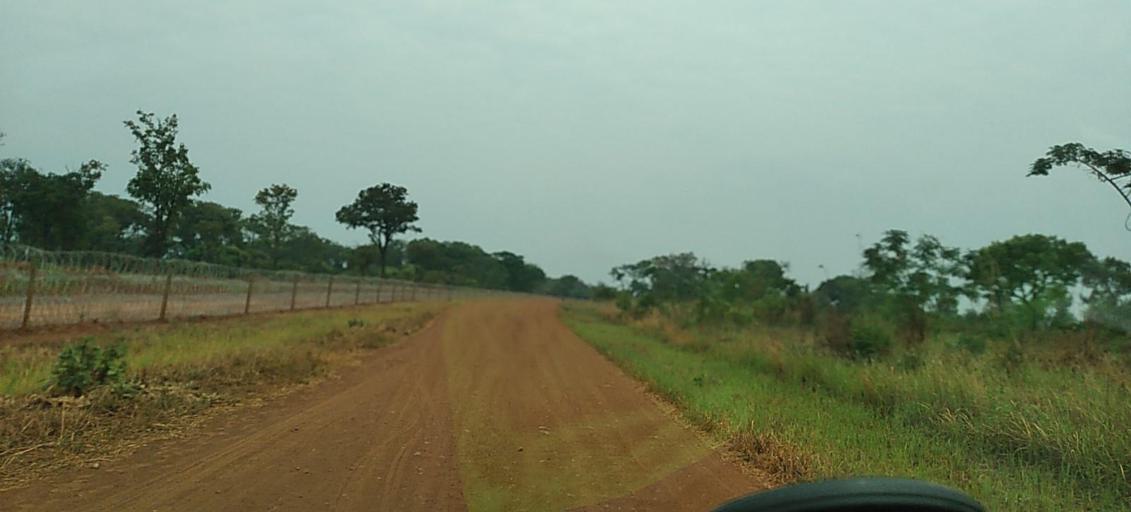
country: ZM
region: North-Western
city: Kansanshi
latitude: -12.0927
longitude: 26.4909
